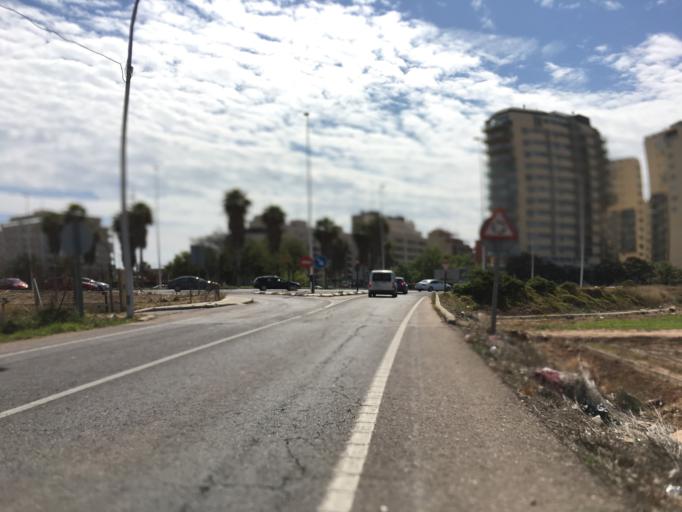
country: ES
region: Valencia
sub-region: Provincia de Valencia
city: Mislata
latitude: 39.4880
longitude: -0.4063
